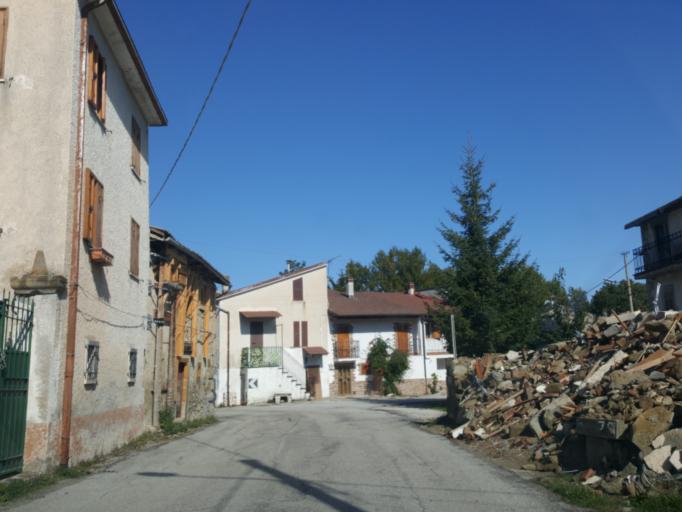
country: IT
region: Abruzzo
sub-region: Provincia dell' Aquila
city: Campotosto
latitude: 42.5602
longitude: 13.3274
